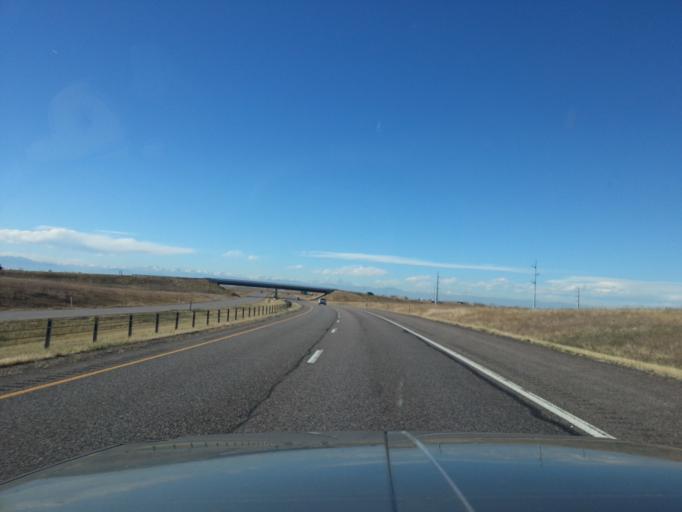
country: US
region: Colorado
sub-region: Adams County
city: Brighton
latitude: 39.9046
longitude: -104.7671
